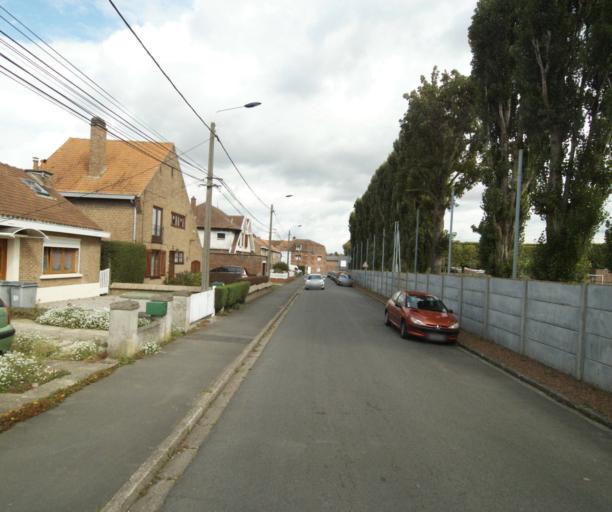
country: FR
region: Nord-Pas-de-Calais
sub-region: Departement du Nord
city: Perenchies
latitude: 50.6672
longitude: 2.9651
